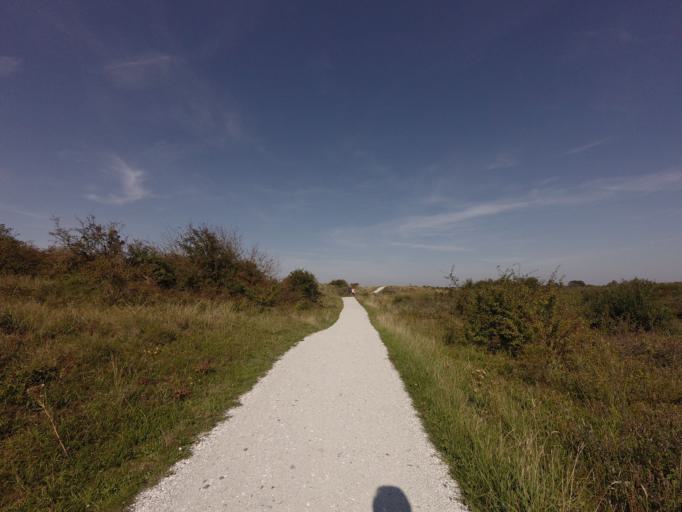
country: NL
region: Friesland
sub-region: Gemeente Schiermonnikoog
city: Schiermonnikoog
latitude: 53.4733
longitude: 6.1423
